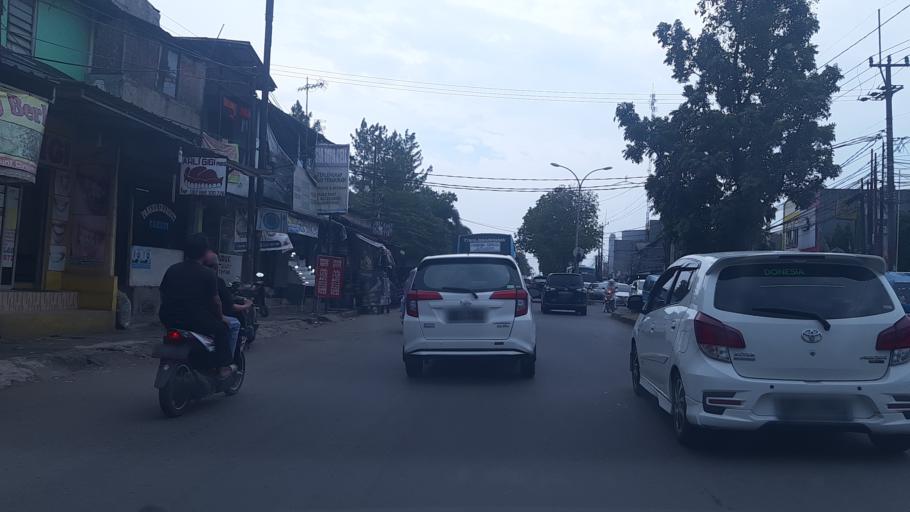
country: ID
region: West Java
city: Cibinong
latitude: -6.4792
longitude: 106.8634
